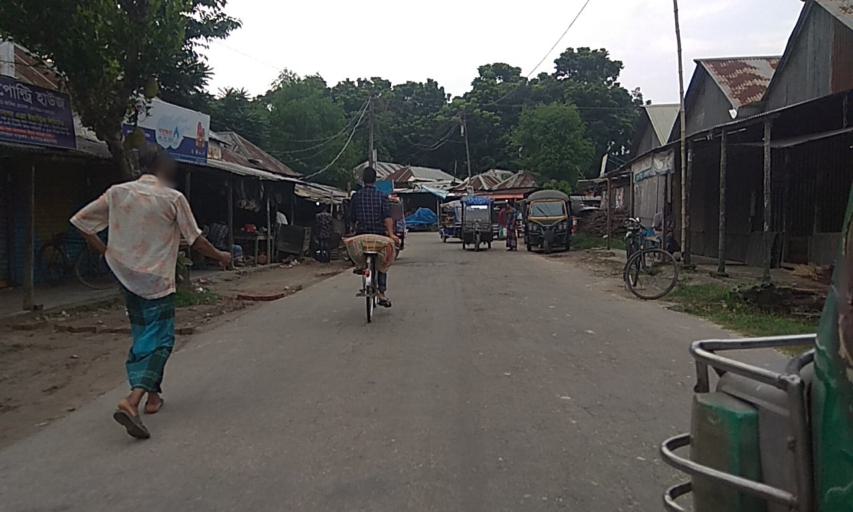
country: BD
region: Dhaka
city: Dohar
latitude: 23.4564
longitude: 90.0055
